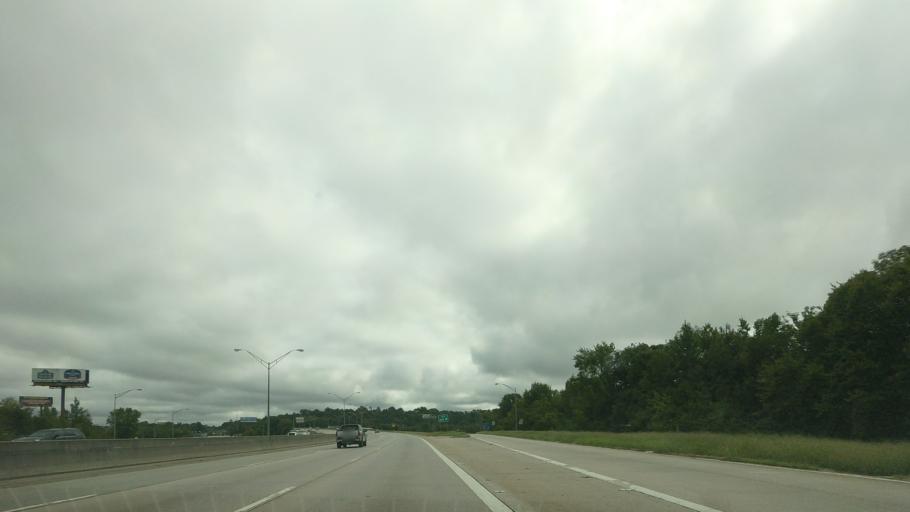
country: US
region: Georgia
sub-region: Bibb County
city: Macon
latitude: 32.7861
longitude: -83.6708
